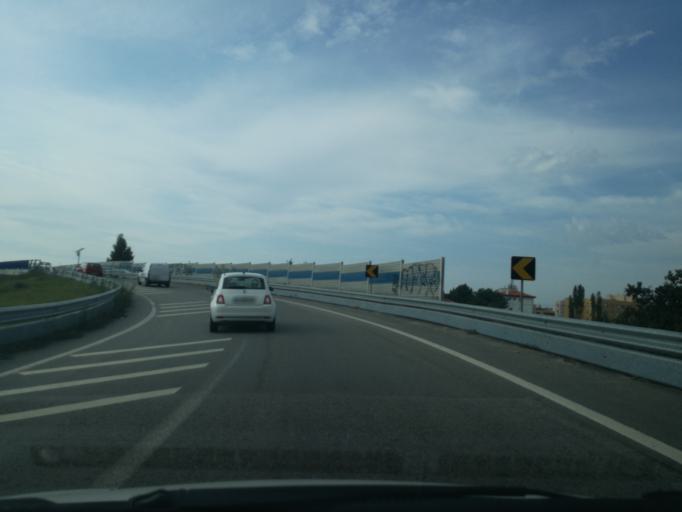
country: PT
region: Porto
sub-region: Vila Nova de Gaia
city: Vila Nova de Gaia
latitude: 41.1160
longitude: -8.6261
